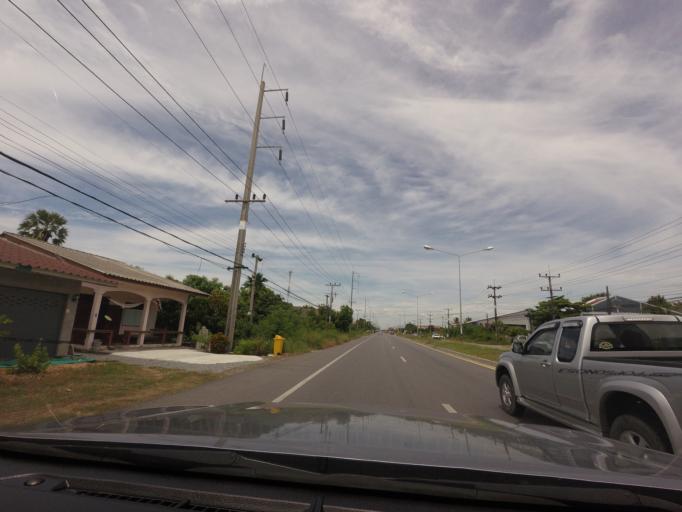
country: TH
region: Songkhla
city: Ranot
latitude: 7.7697
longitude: 100.3569
